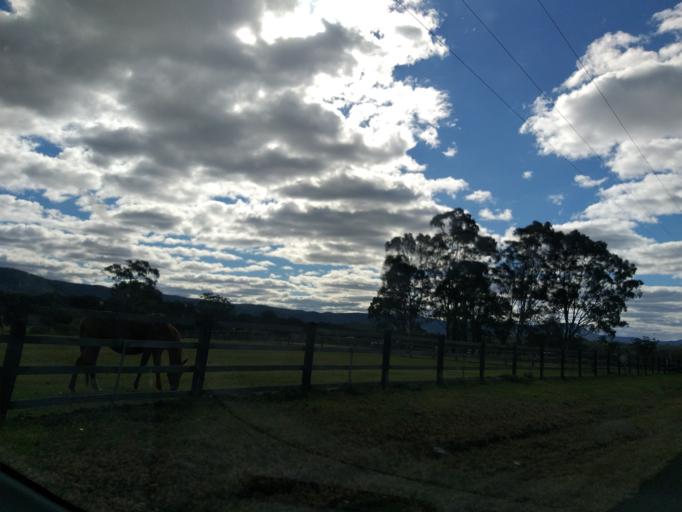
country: AU
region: New South Wales
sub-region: Shellharbour
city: Albion Park Rail
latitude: -34.5355
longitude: 150.7681
